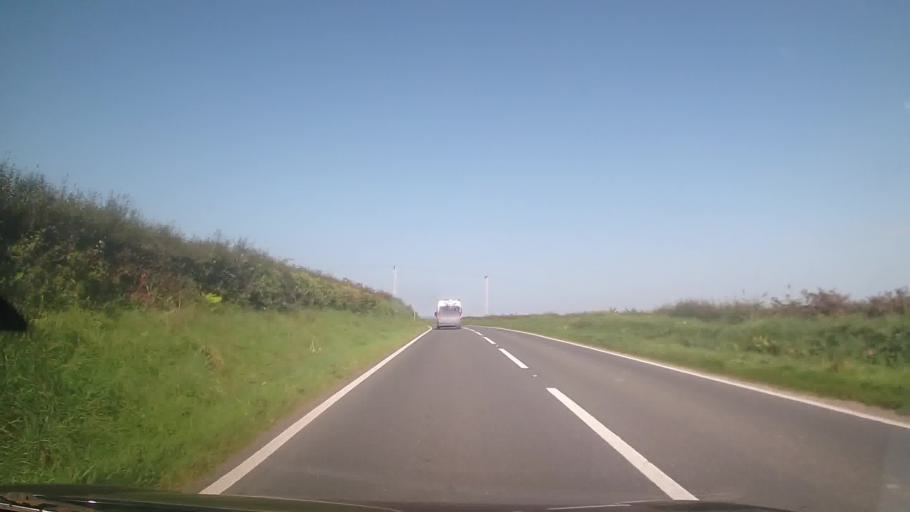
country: GB
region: Wales
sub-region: County of Ceredigion
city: Cardigan
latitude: 52.0563
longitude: -4.6880
